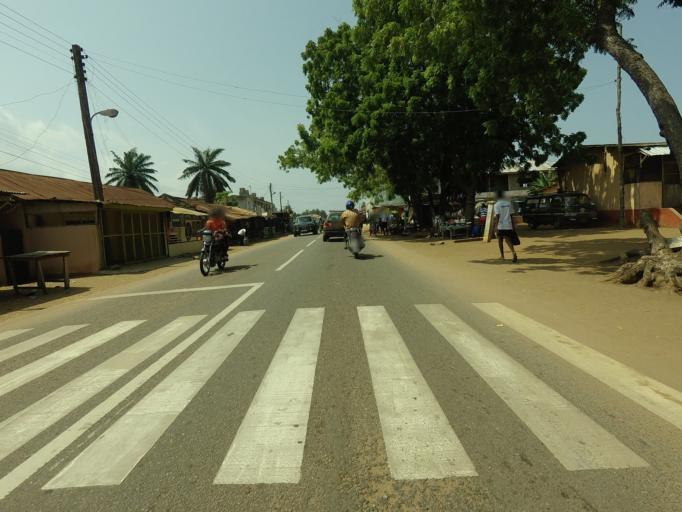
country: TG
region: Maritime
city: Lome
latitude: 6.1007
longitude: 1.1470
